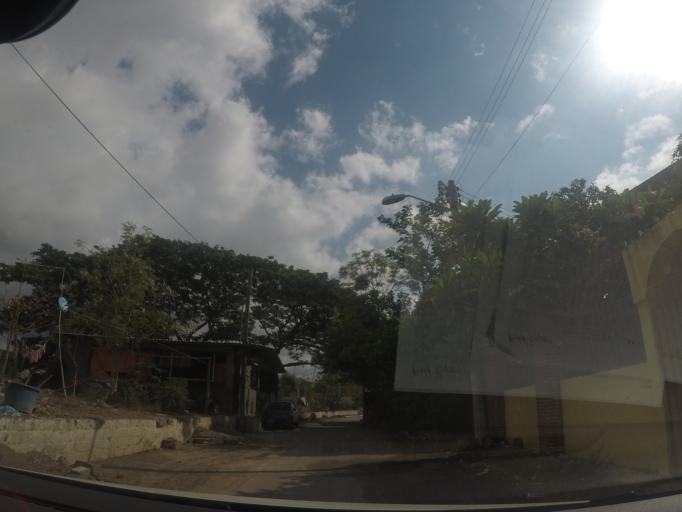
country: MX
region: Oaxaca
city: Juchitan de Zaragoza
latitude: 16.4308
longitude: -95.0255
